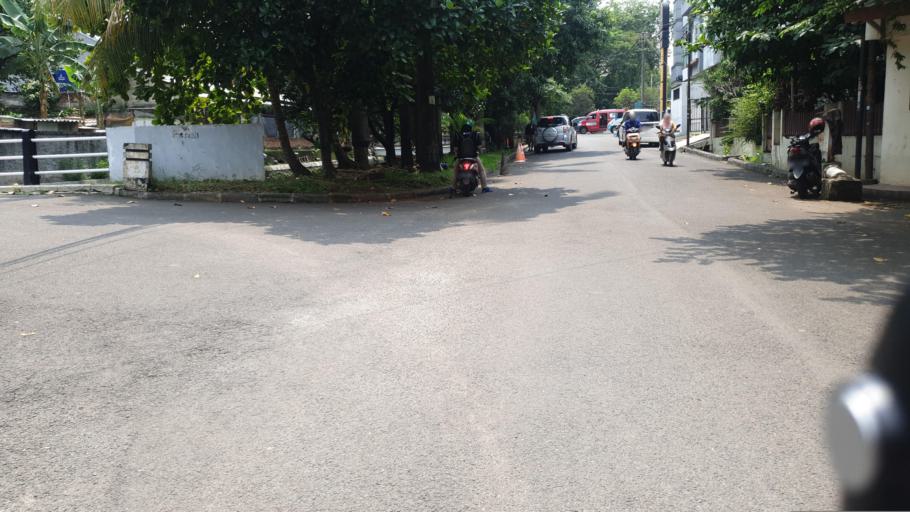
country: ID
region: West Java
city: Ciputat
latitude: -6.1969
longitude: 106.7460
